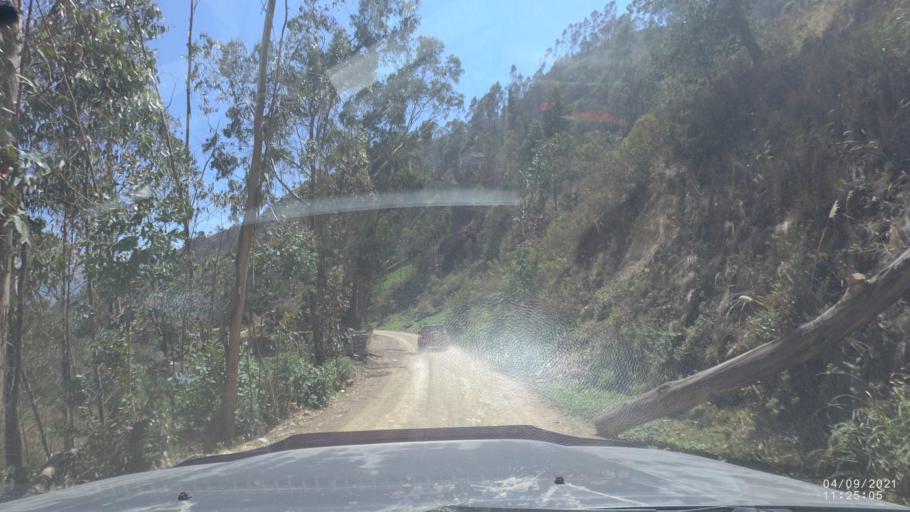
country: BO
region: Cochabamba
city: Colchani
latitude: -17.2577
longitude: -66.5109
